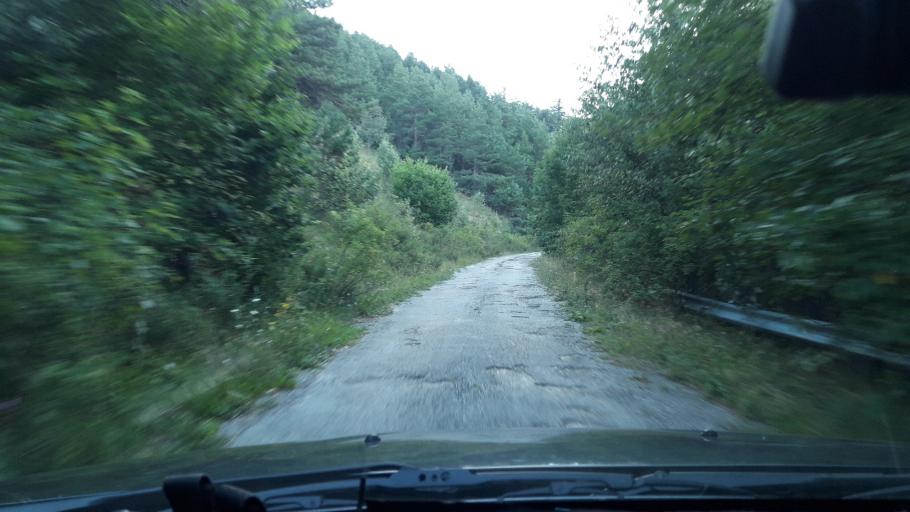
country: FR
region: Rhone-Alpes
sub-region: Departement de l'Isere
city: Mens
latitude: 44.7254
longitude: 5.6721
